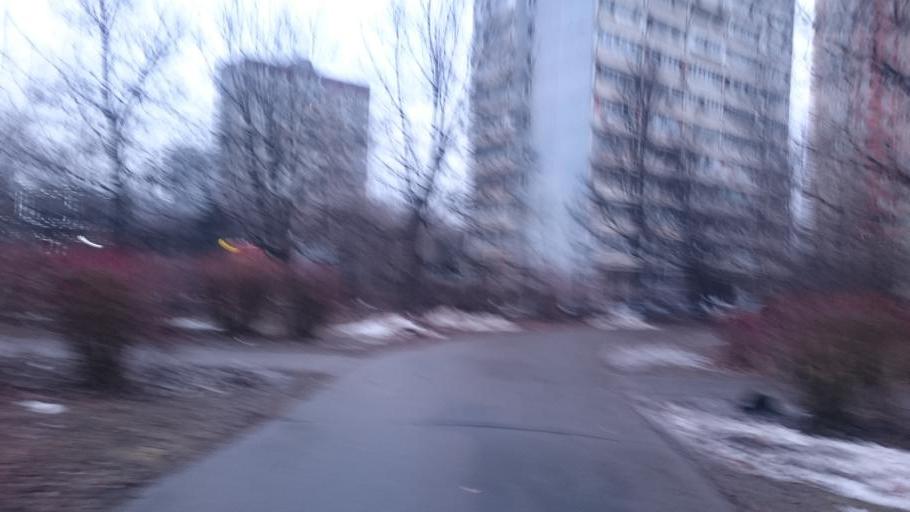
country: RU
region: Moskovskaya
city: Novoivanovskoye
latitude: 55.7037
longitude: 37.3618
